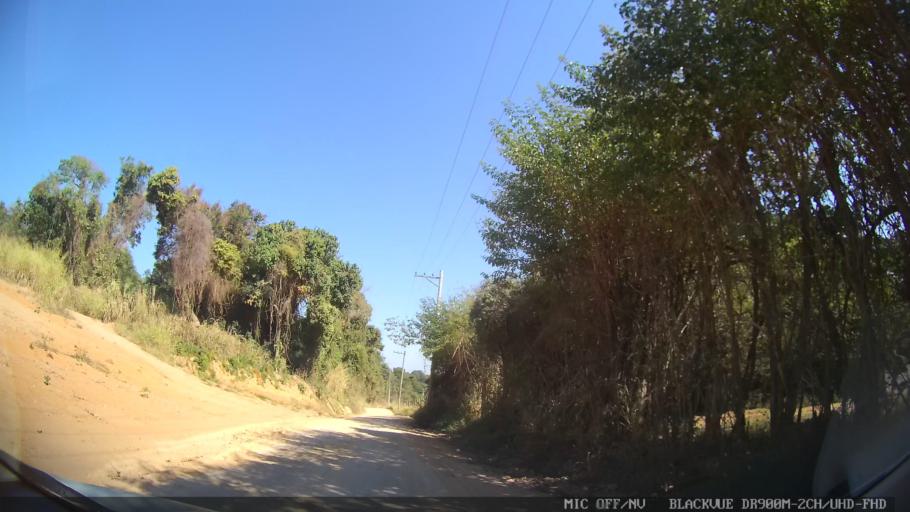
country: BR
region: Sao Paulo
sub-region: Itupeva
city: Itupeva
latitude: -23.1098
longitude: -47.0567
